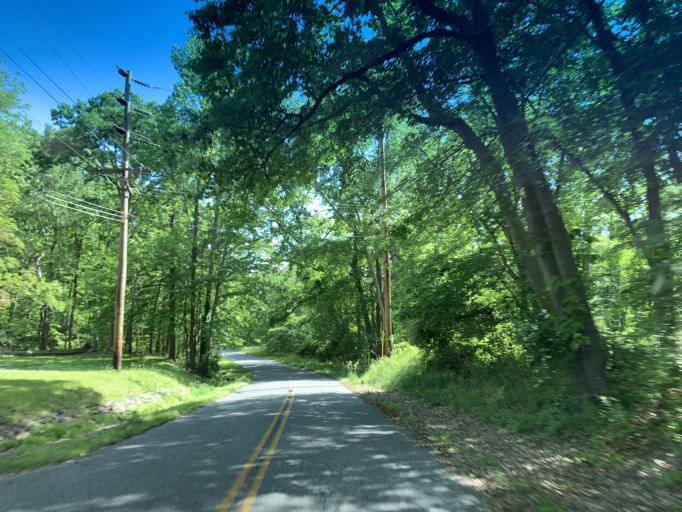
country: US
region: Maryland
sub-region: Cecil County
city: Charlestown
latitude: 39.5454
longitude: -75.9475
